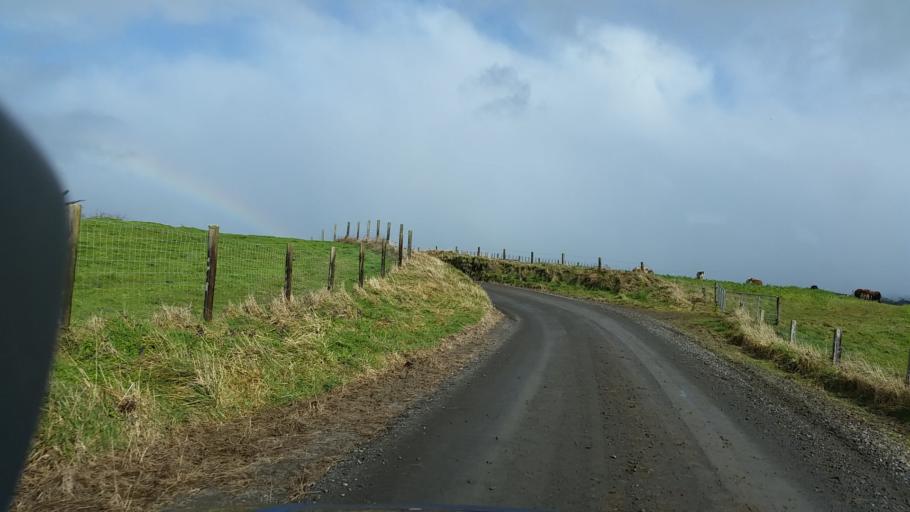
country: NZ
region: Taranaki
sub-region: South Taranaki District
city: Eltham
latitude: -39.2802
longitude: 174.3083
